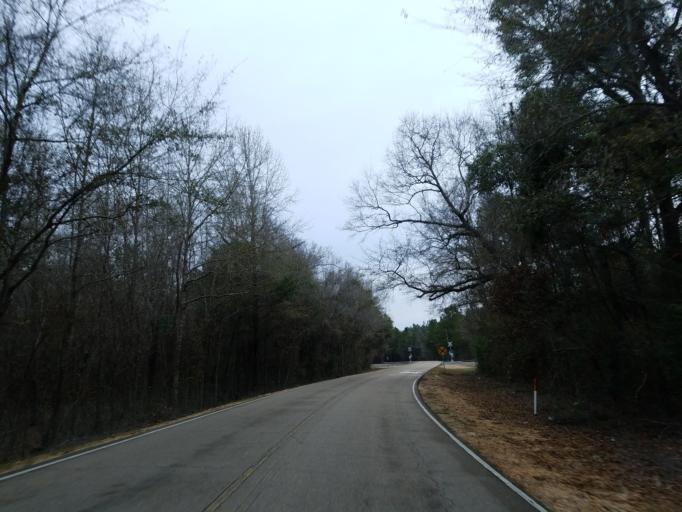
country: US
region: Mississippi
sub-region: Forrest County
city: Hattiesburg
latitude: 31.2534
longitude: -89.2330
